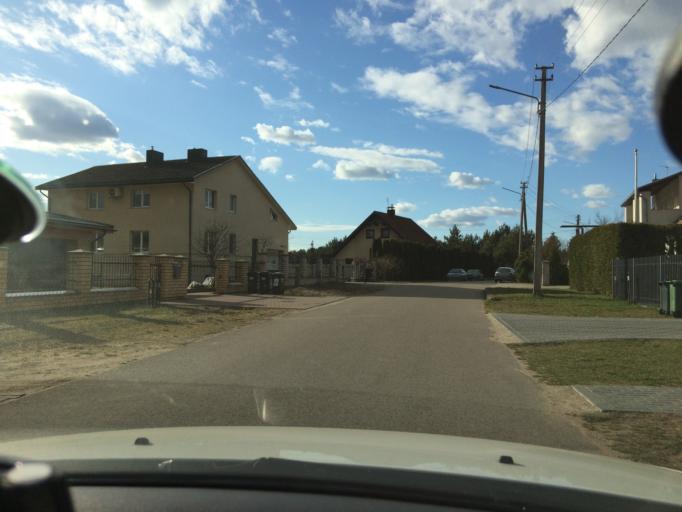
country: LT
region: Vilnius County
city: Rasos
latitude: 54.7763
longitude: 25.3481
